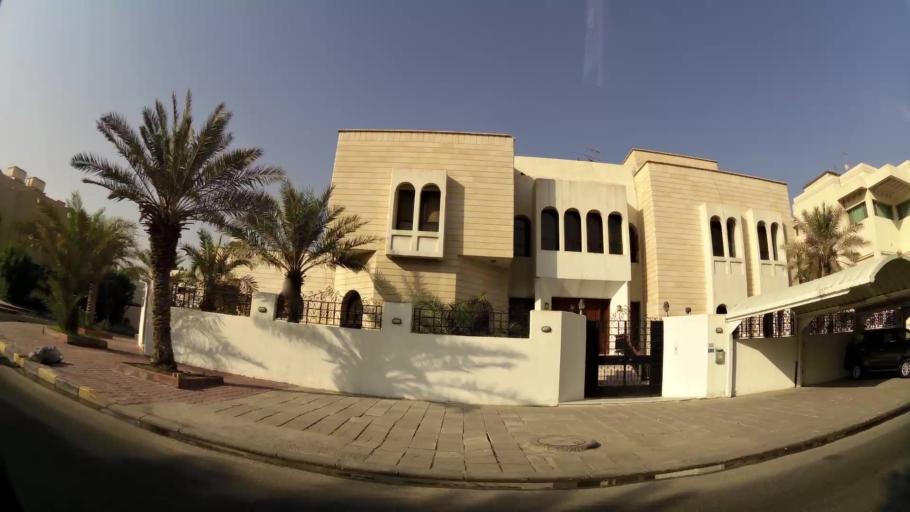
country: KW
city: Bayan
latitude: 29.3121
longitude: 48.0408
